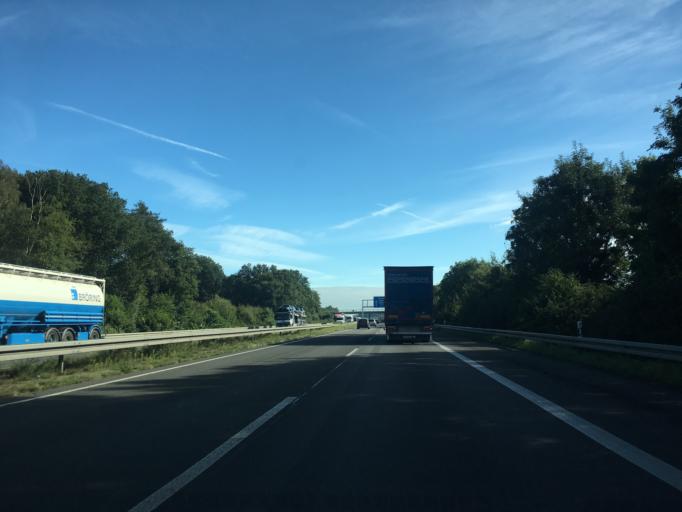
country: DE
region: North Rhine-Westphalia
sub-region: Regierungsbezirk Munster
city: Ladbergen
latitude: 52.1062
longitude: 7.6884
